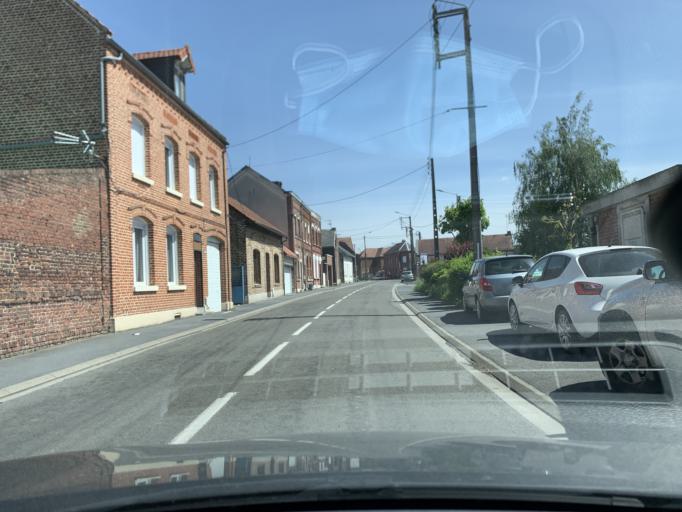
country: FR
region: Nord-Pas-de-Calais
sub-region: Departement du Nord
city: Masnieres
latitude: 50.1172
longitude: 3.2078
